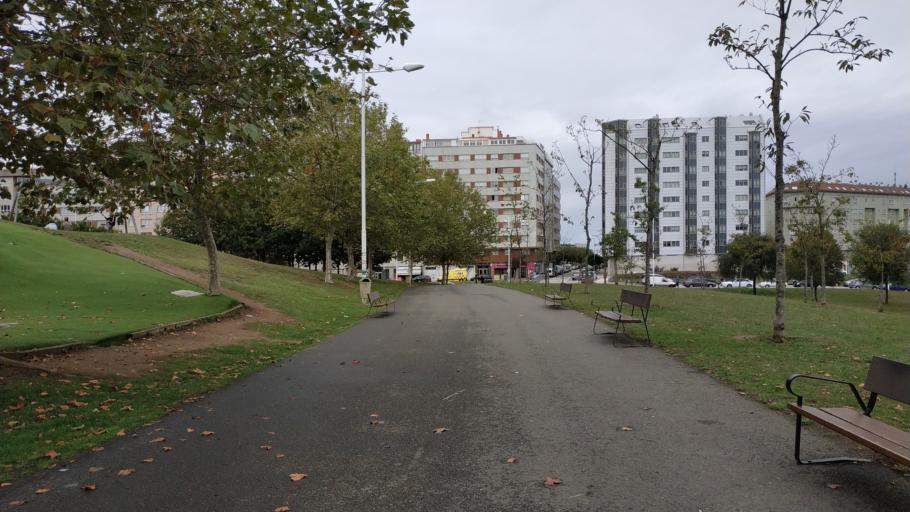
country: ES
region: Galicia
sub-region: Provincia da Coruna
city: A Coruna
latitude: 43.3463
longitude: -8.3956
